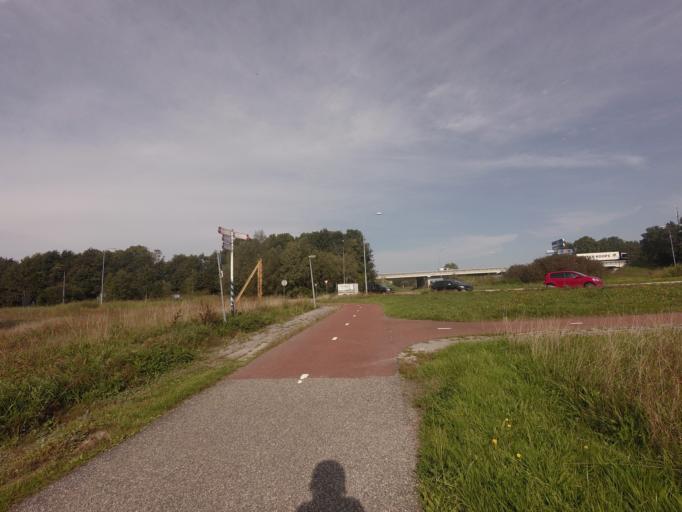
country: NL
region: Groningen
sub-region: Gemeente Leek
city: Leek
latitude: 53.1840
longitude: 6.3790
